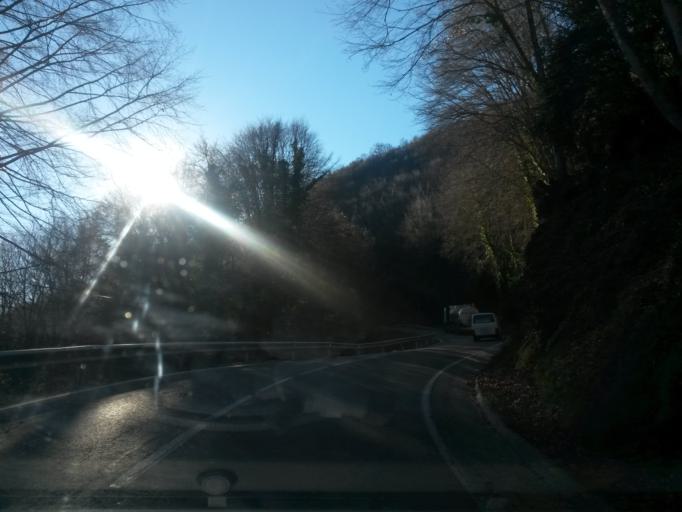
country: ES
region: Catalonia
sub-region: Provincia de Girona
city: Sant Feliu de Pallerols
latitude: 42.0528
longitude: 2.5073
